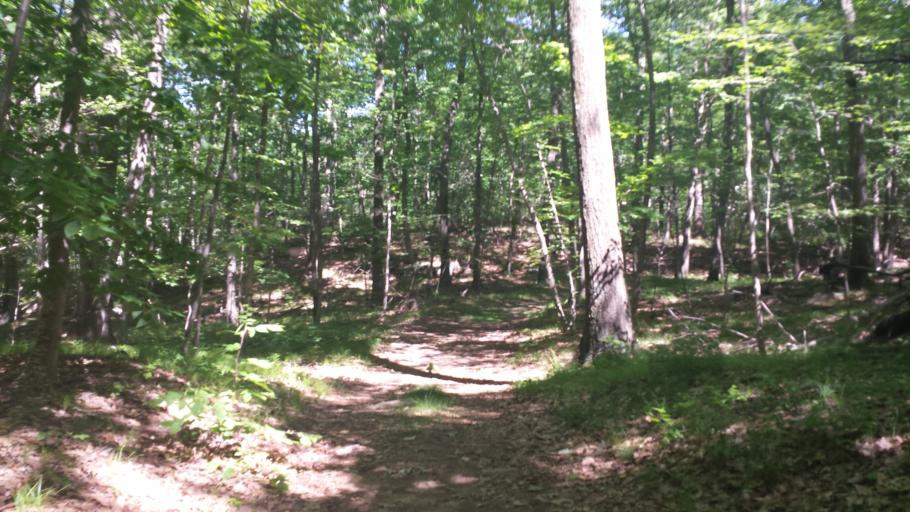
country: US
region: New York
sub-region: Westchester County
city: Pound Ridge
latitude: 41.2325
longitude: -73.5941
